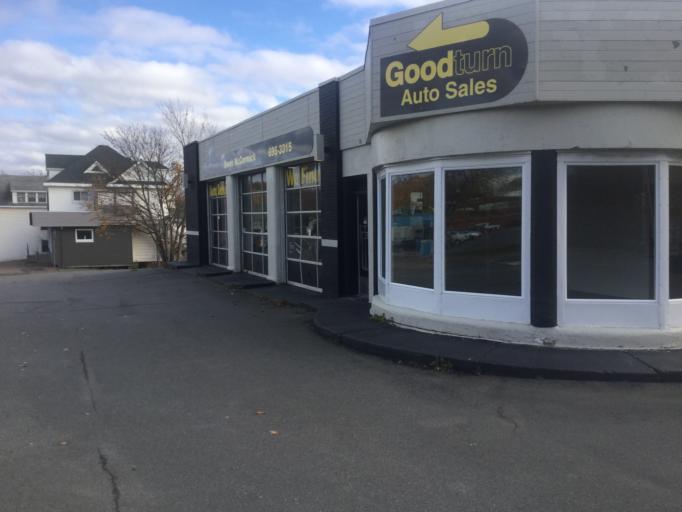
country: CA
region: Nova Scotia
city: New Glasgow
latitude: 45.5900
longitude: -62.6497
